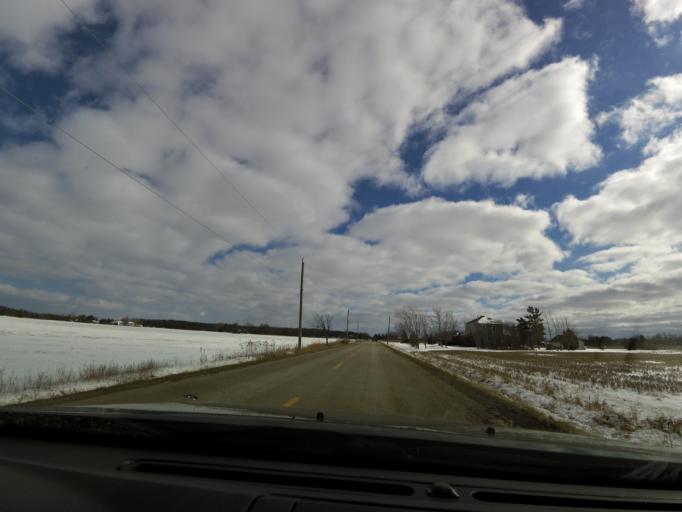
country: CA
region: Ontario
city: Hamilton
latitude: 43.1135
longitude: -79.6457
